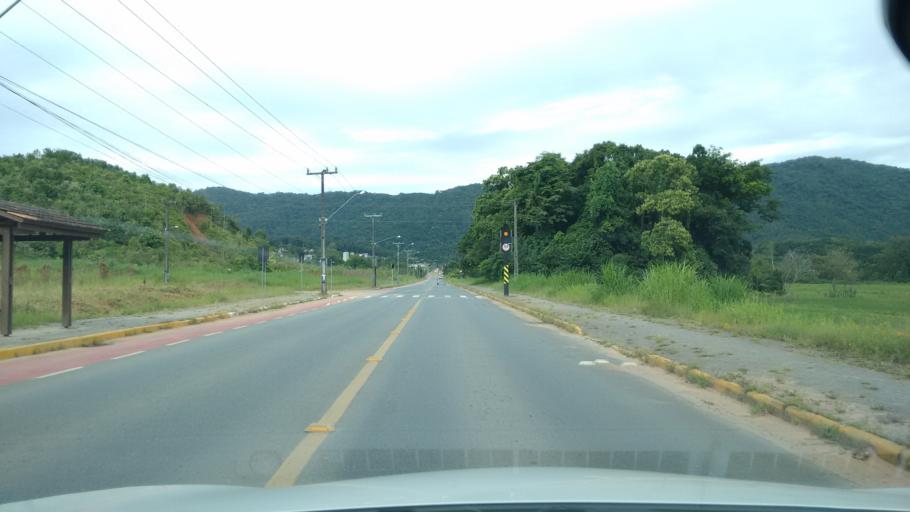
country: BR
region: Santa Catarina
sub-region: Timbo
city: Timbo
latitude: -26.8086
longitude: -49.2579
